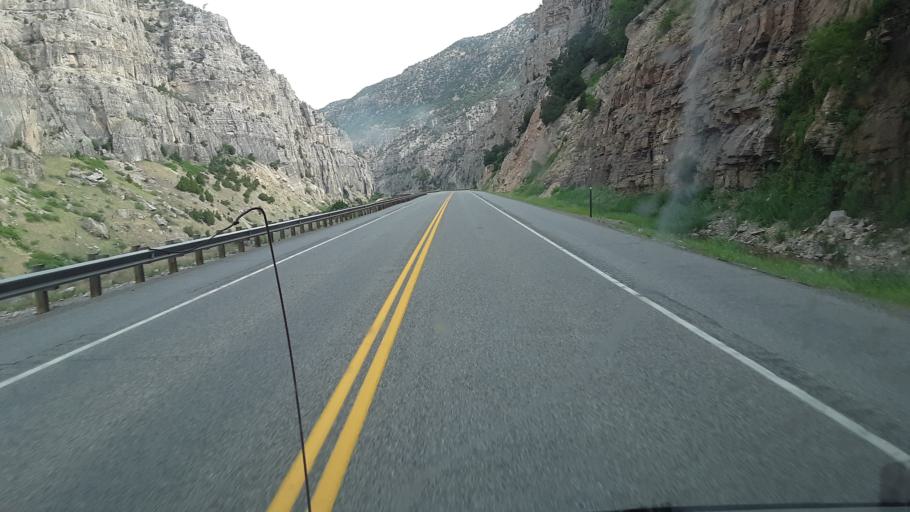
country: US
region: Wyoming
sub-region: Hot Springs County
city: Thermopolis
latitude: 43.5312
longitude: -108.1784
